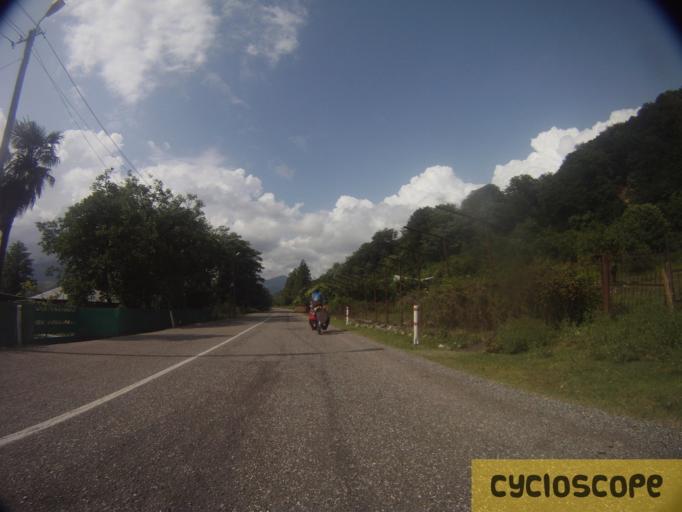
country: GE
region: Samegrelo and Zemo Svaneti
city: Tsalenjikha
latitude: 42.6207
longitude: 41.9704
